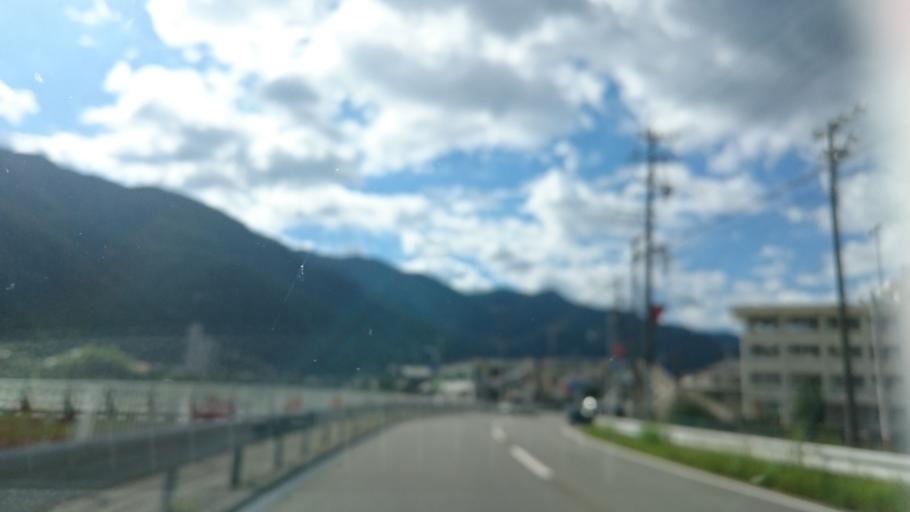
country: JP
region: Gifu
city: Gujo
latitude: 35.7987
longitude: 137.2522
